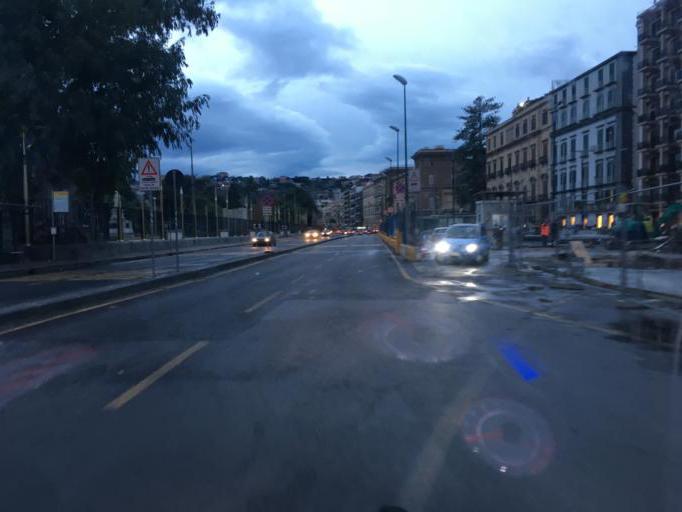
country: IT
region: Campania
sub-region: Provincia di Napoli
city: Napoli
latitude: 40.8335
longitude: 14.2358
